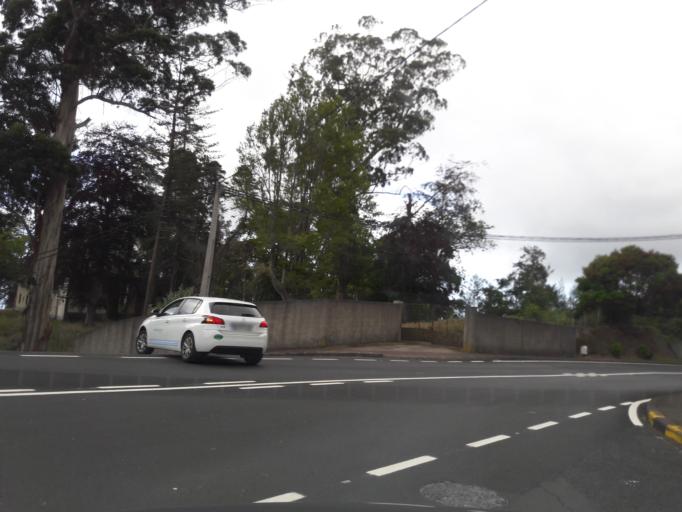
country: PT
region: Madeira
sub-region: Santa Cruz
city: Camacha
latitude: 32.6773
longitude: -16.8452
